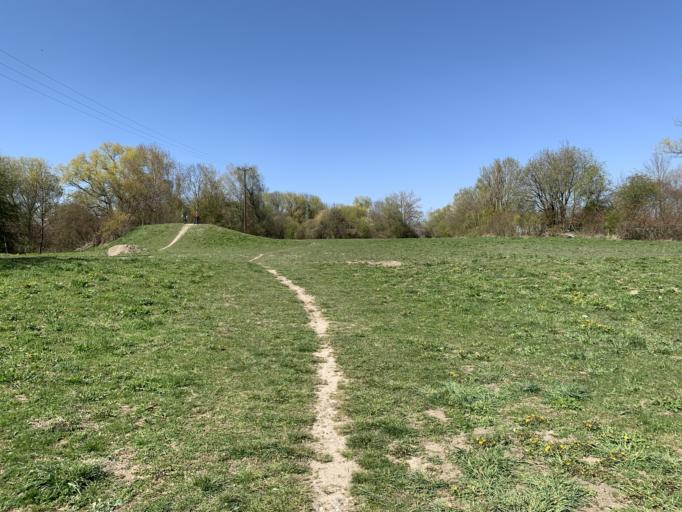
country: DE
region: Bavaria
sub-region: Swabia
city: Gersthofen
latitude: 48.4166
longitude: 10.8861
